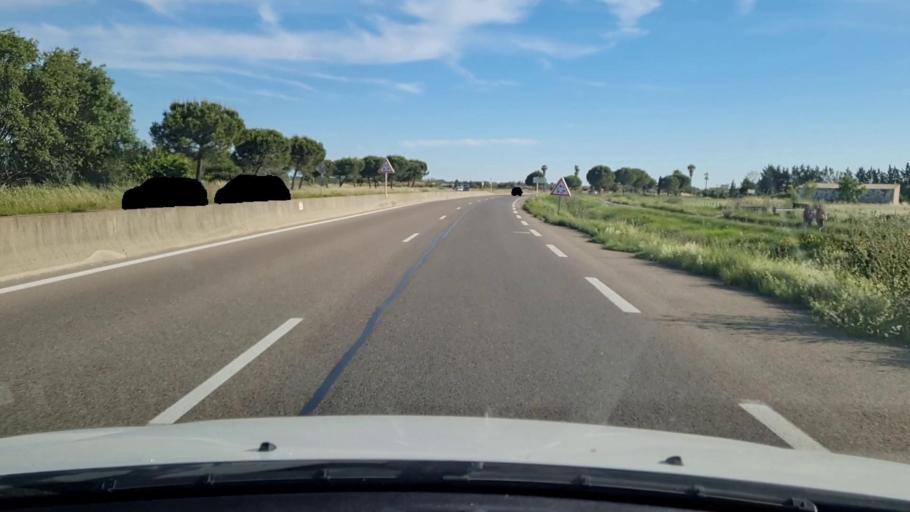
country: FR
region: Languedoc-Roussillon
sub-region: Departement du Gard
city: Aigues-Mortes
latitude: 43.6149
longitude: 4.1925
